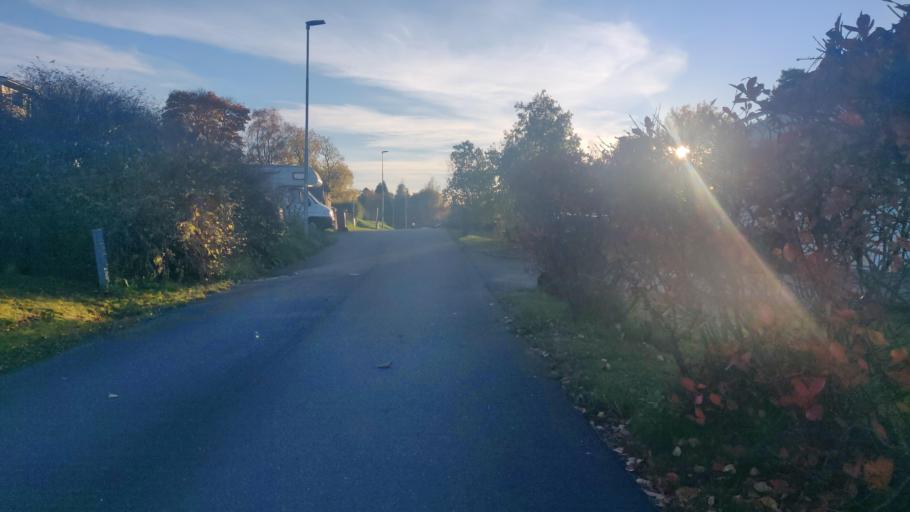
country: SE
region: Vaesternorrland
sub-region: Sundsvalls Kommun
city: Njurundabommen
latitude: 62.2666
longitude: 17.3826
